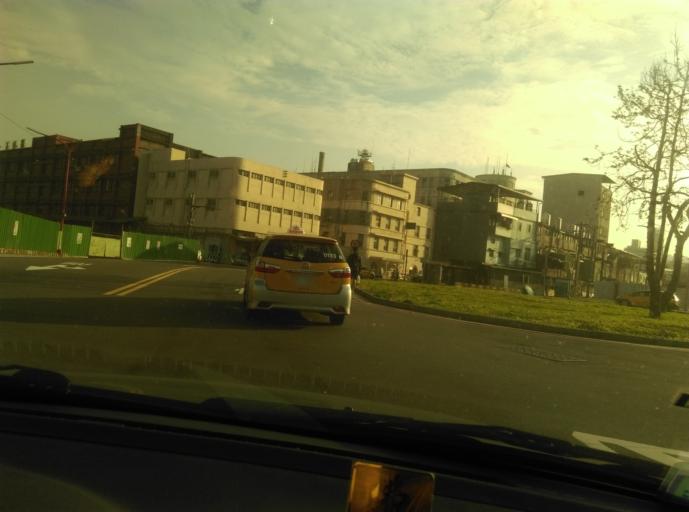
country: TW
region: Taiwan
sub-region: Keelung
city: Keelung
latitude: 25.1345
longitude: 121.7406
